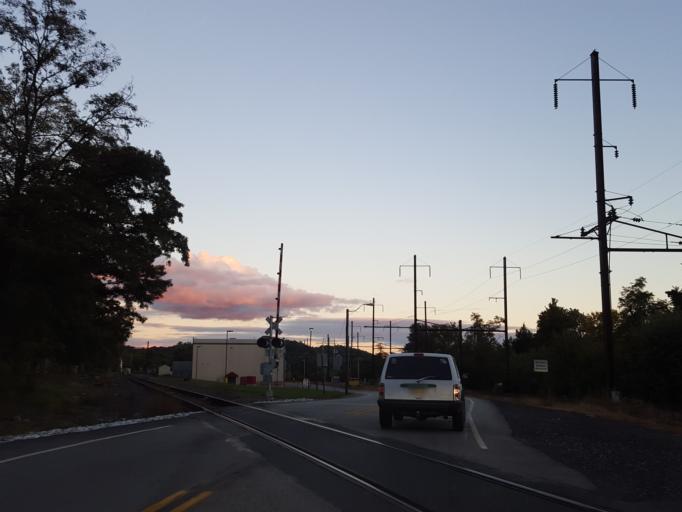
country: US
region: Pennsylvania
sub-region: Lancaster County
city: Columbia
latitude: 40.0295
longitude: -76.5049
